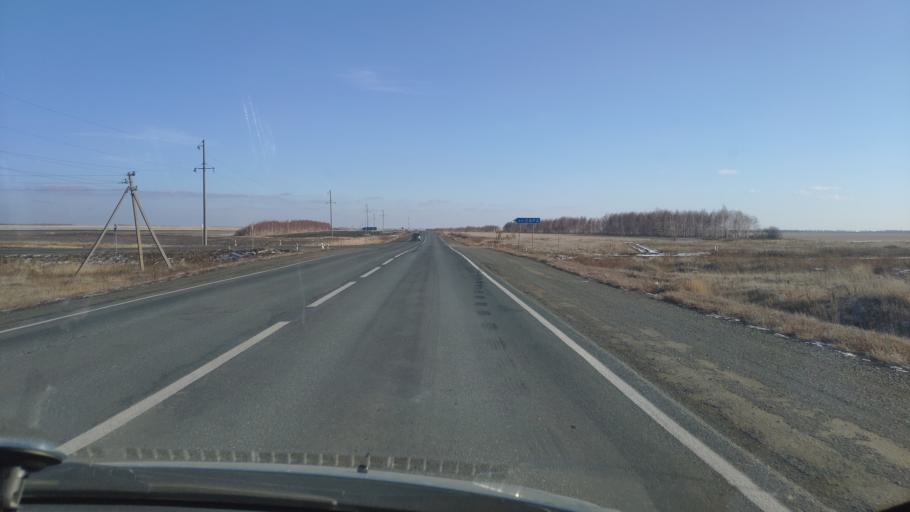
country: RU
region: Orenburg
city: Novorudnyy
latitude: 51.4325
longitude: 57.9103
